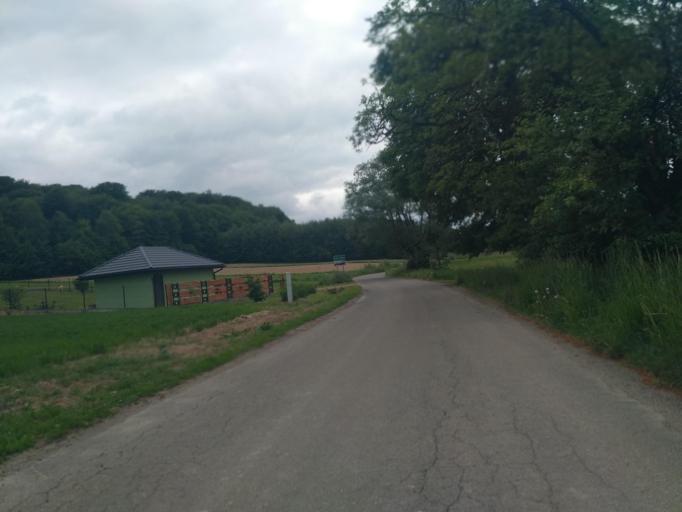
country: PL
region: Subcarpathian Voivodeship
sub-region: Powiat jasielski
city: Tarnowiec
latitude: 49.6899
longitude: 21.5848
